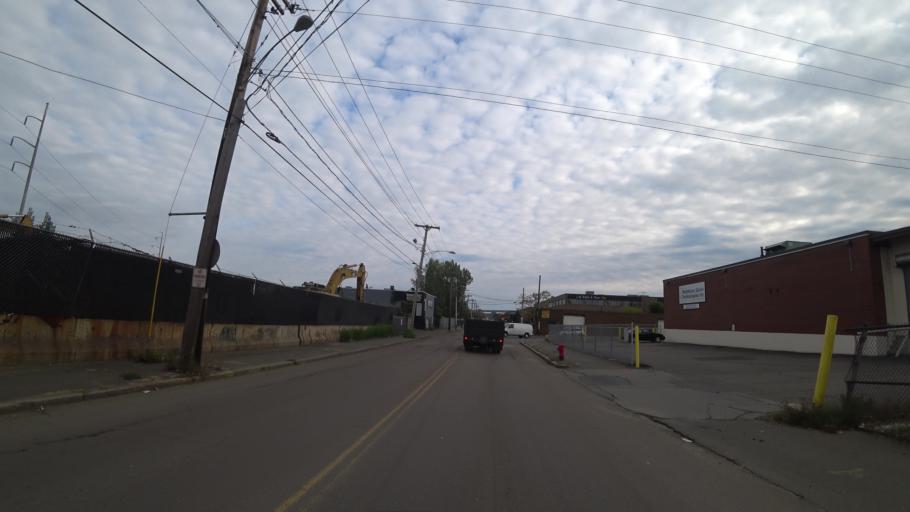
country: US
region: Massachusetts
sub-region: Middlesex County
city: Everett
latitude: 42.3979
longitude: -71.0476
